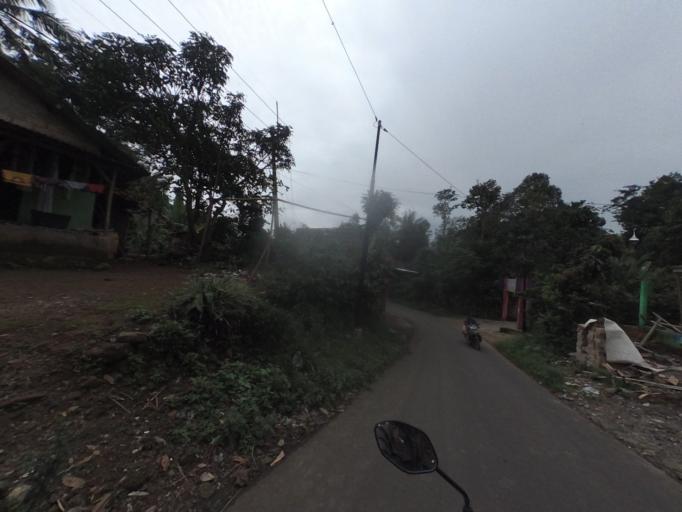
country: ID
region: West Java
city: Bogor
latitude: -6.6388
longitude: 106.7401
